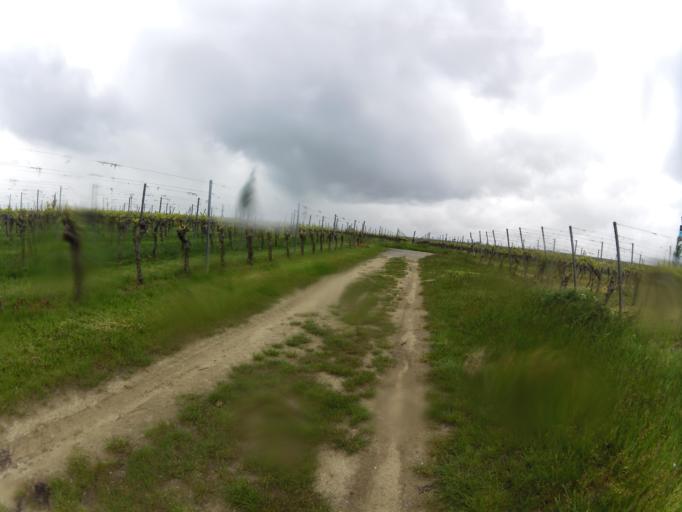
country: DE
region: Bavaria
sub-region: Regierungsbezirk Unterfranken
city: Sommerach
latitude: 49.8432
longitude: 10.2063
